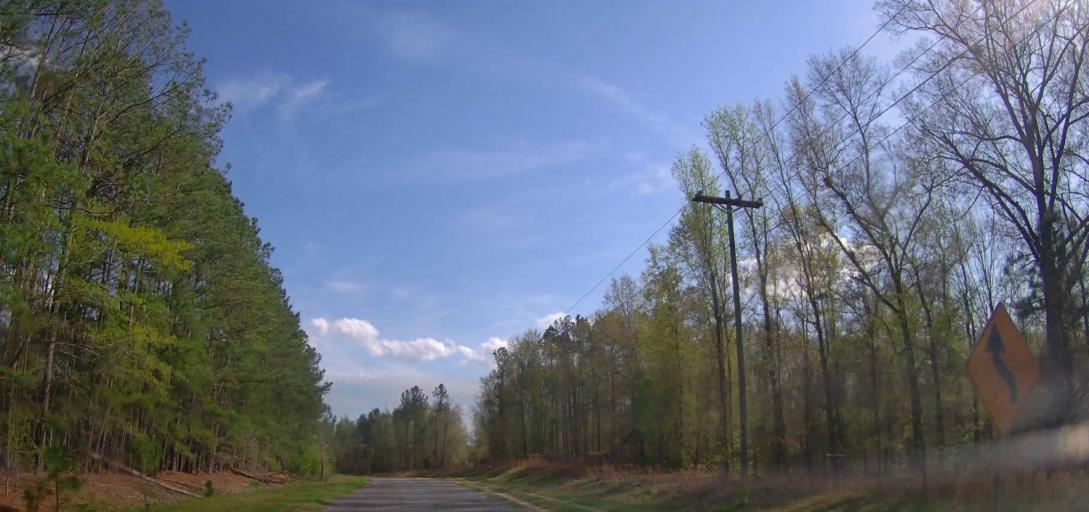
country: US
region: Georgia
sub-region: Baldwin County
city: Hardwick
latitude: 33.0292
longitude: -83.1191
